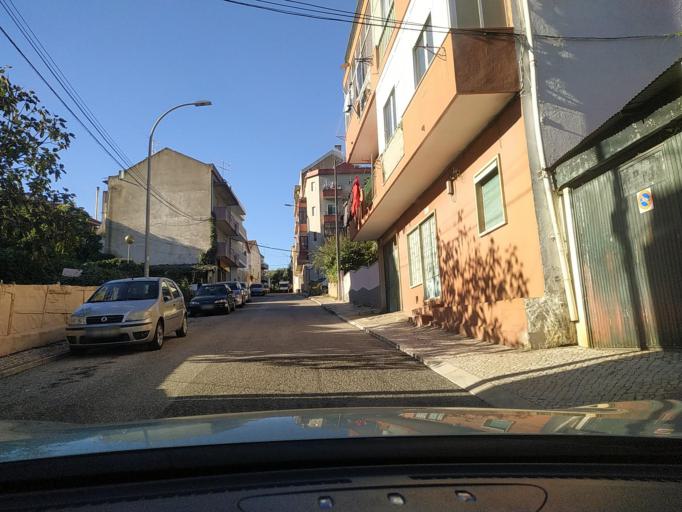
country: PT
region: Lisbon
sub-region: Odivelas
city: Pontinha
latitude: 38.7708
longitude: -9.2150
